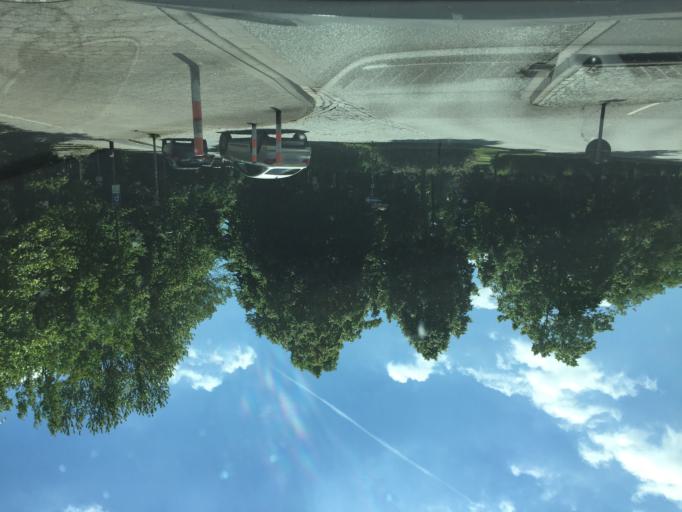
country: DE
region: Schleswig-Holstein
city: Flensburg
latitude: 54.7776
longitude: 9.4381
